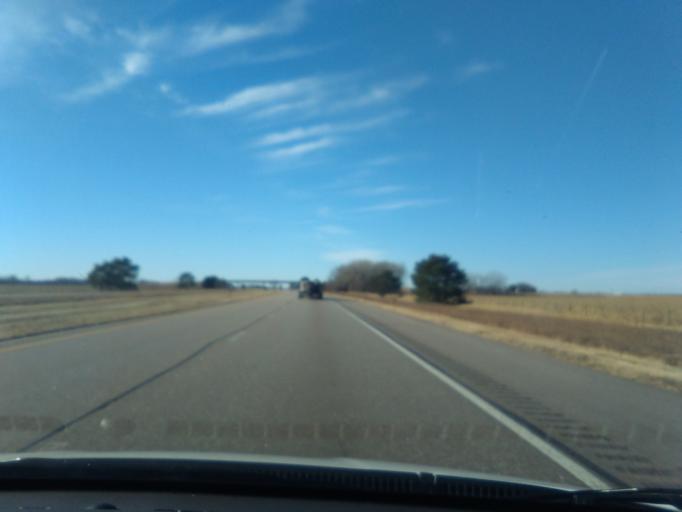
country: US
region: Nebraska
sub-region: Hall County
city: Wood River
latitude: 40.7952
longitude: -98.5063
